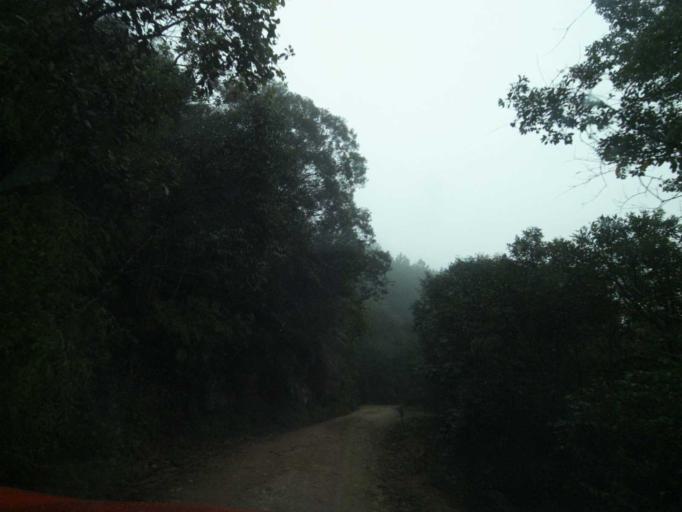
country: BR
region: Santa Catarina
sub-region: Anitapolis
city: Anitapolis
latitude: -27.9214
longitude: -49.2040
